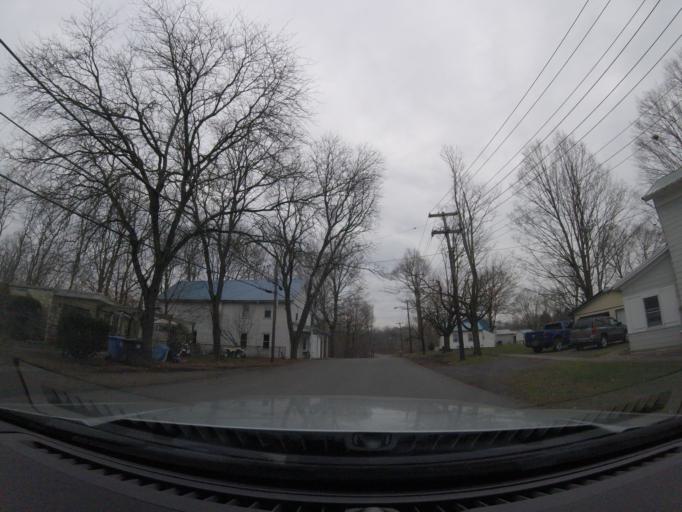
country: US
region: New York
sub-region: Yates County
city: Penn Yan
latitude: 42.6823
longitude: -76.9541
